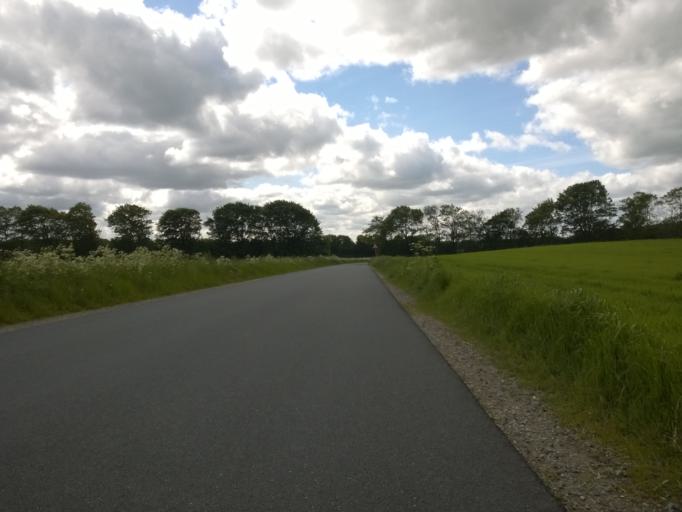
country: DK
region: Central Jutland
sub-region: Holstebro Kommune
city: Vinderup
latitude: 56.4039
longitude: 8.7809
